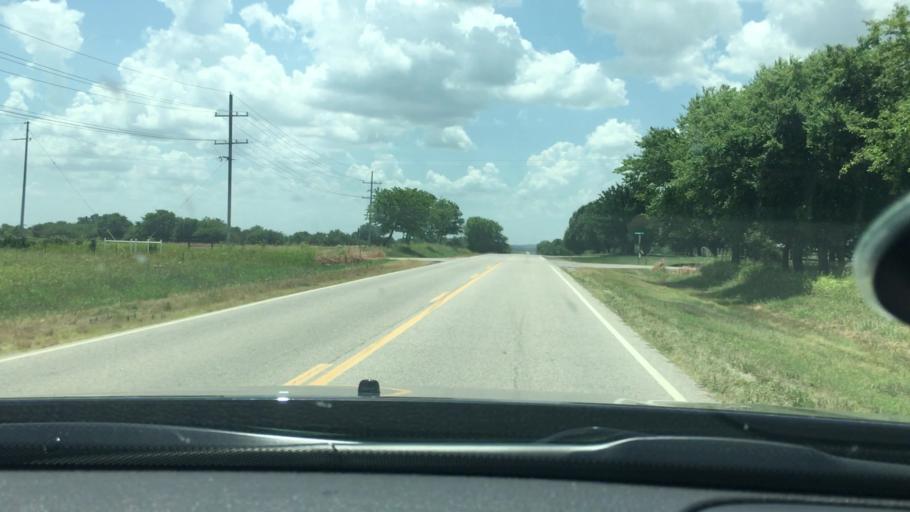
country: US
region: Oklahoma
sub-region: Pontotoc County
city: Ada
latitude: 34.6661
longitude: -96.6349
